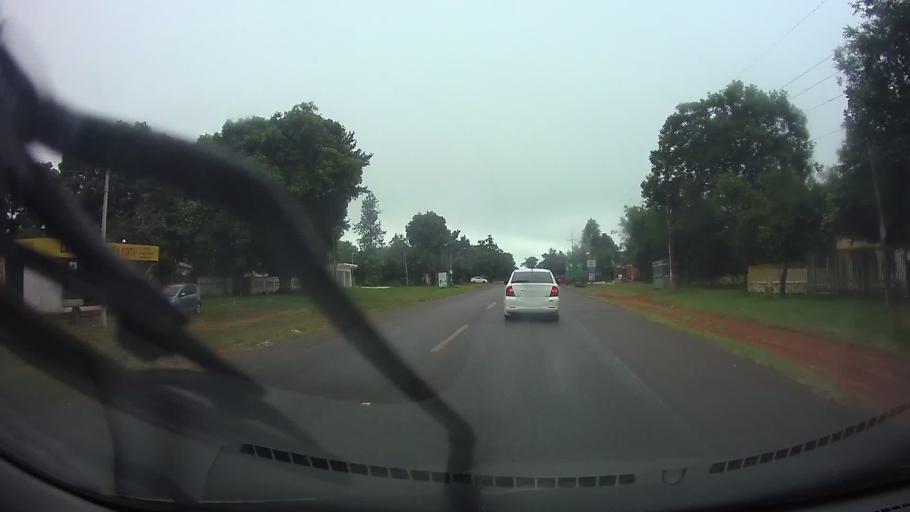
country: PY
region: Central
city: Ita
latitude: -25.5239
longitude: -57.3440
